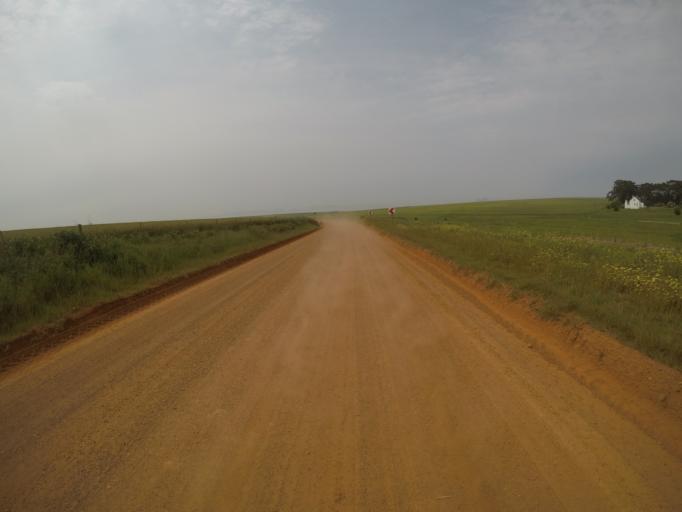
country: ZA
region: Western Cape
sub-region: City of Cape Town
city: Kraaifontein
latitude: -33.7244
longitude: 18.6631
